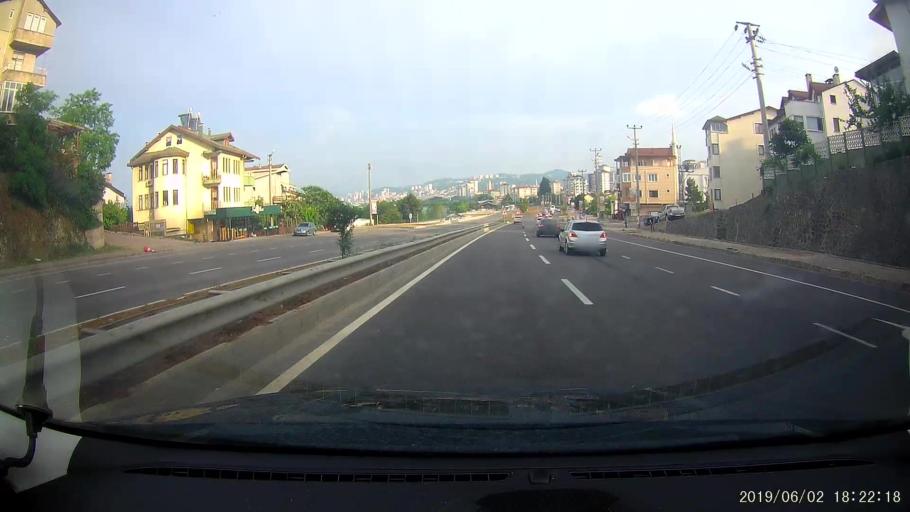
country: TR
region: Ordu
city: Fatsa
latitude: 41.0588
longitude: 37.4767
